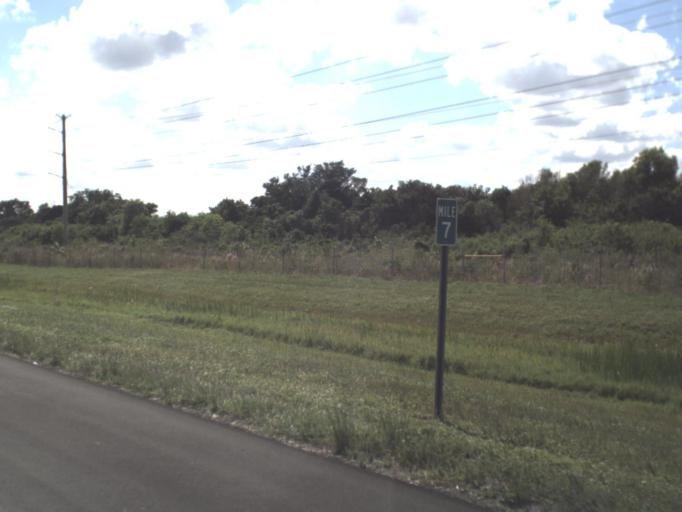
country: US
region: Florida
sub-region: Broward County
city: Tamarac
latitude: 26.2158
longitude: -80.2967
